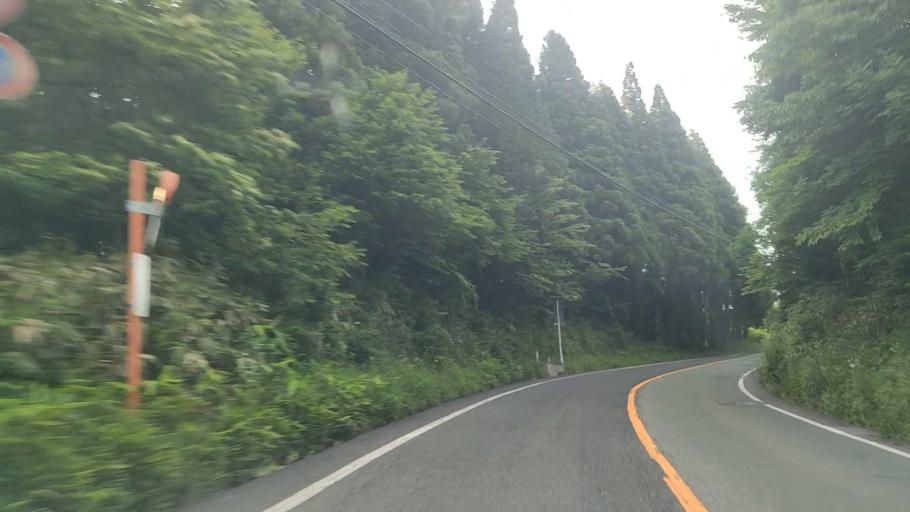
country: JP
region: Tottori
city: Kurayoshi
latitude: 35.2845
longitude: 133.6371
